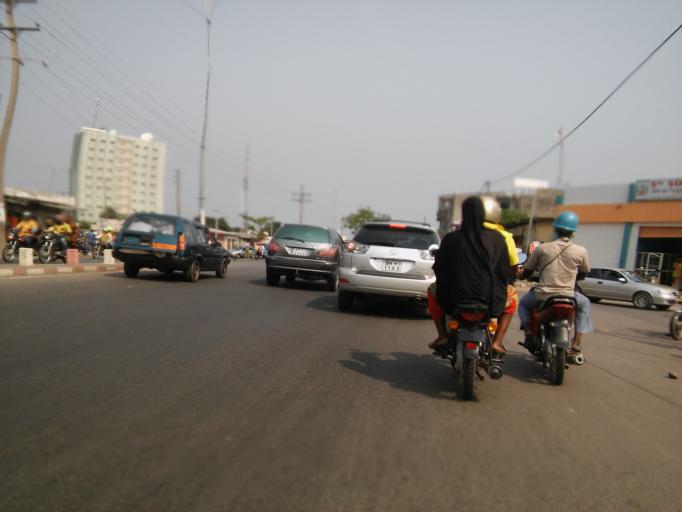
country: BJ
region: Littoral
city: Cotonou
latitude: 6.3702
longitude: 2.4238
